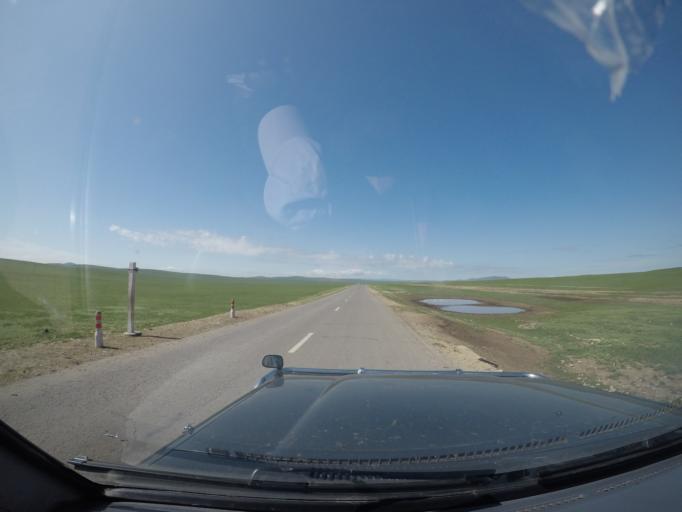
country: MN
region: Suhbaatar
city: Bayasgalant
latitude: 47.3479
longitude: 111.6309
